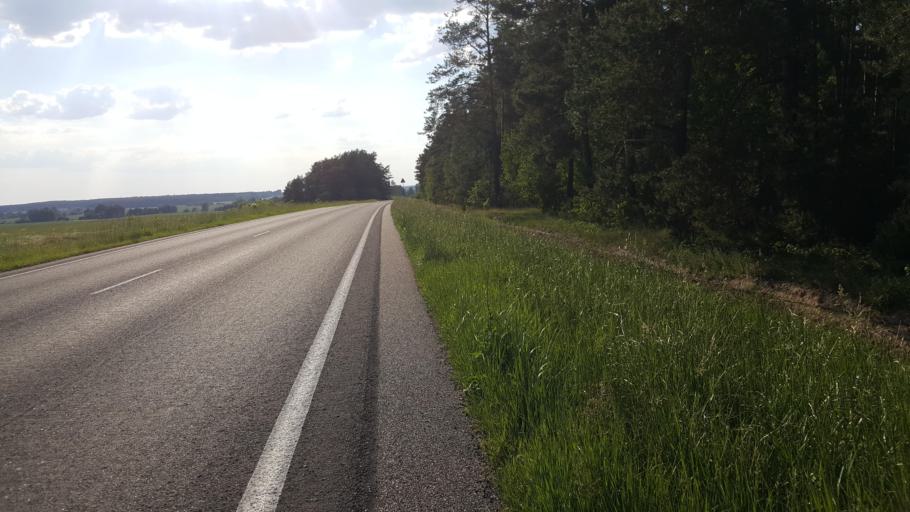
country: BY
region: Brest
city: Kamyanyets
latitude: 52.3974
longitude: 23.9135
